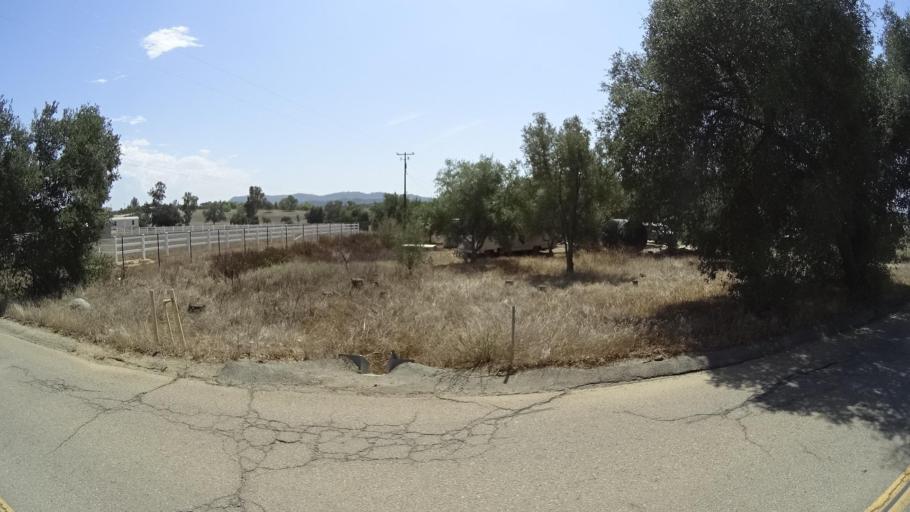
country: US
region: California
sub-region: San Diego County
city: Valley Center
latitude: 33.2422
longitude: -117.0152
